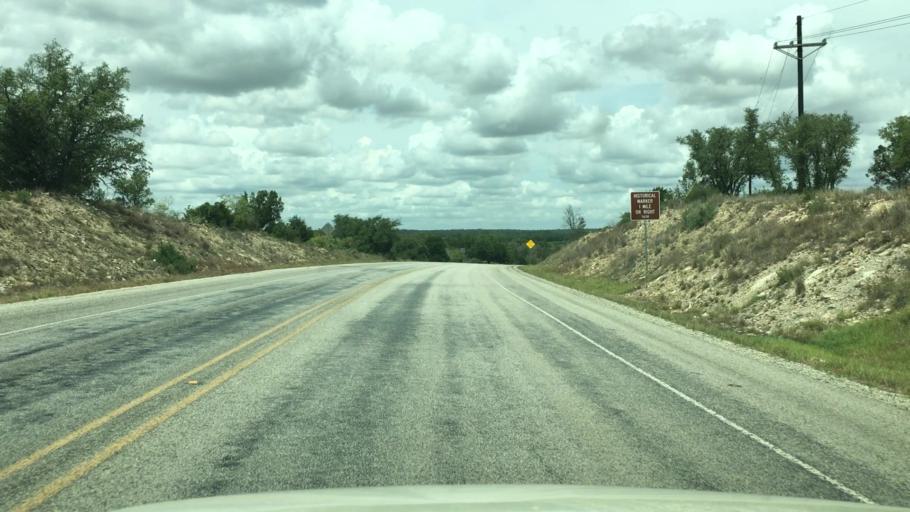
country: US
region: Texas
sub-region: McCulloch County
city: Brady
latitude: 31.0097
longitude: -99.2069
